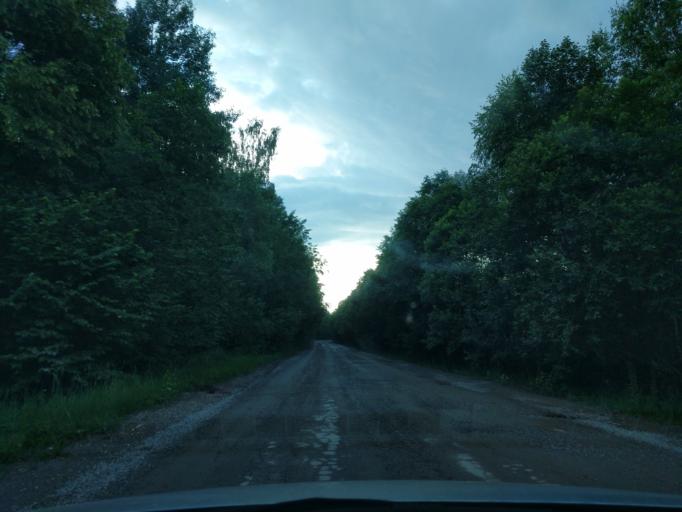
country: RU
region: Kaluga
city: Myatlevo
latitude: 54.8592
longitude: 35.5752
